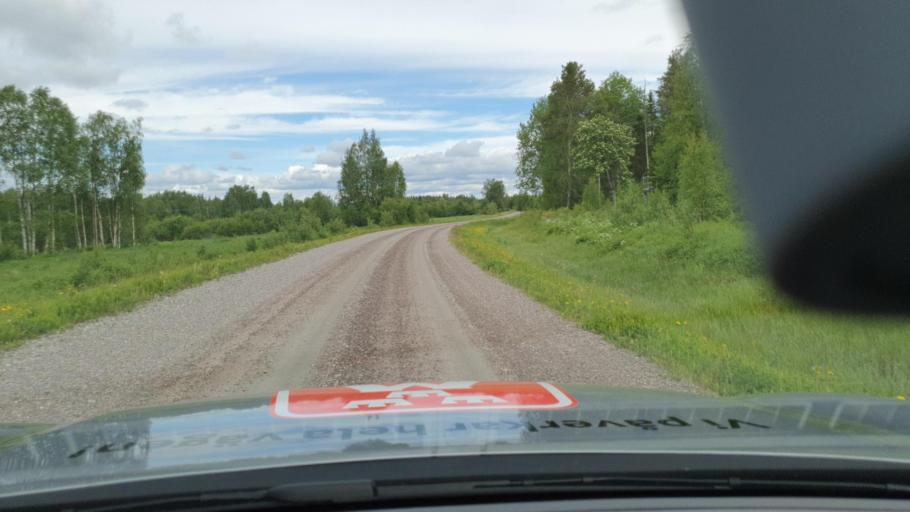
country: FI
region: Lapland
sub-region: Torniolaakso
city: Ylitornio
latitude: 65.9717
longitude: 23.7922
